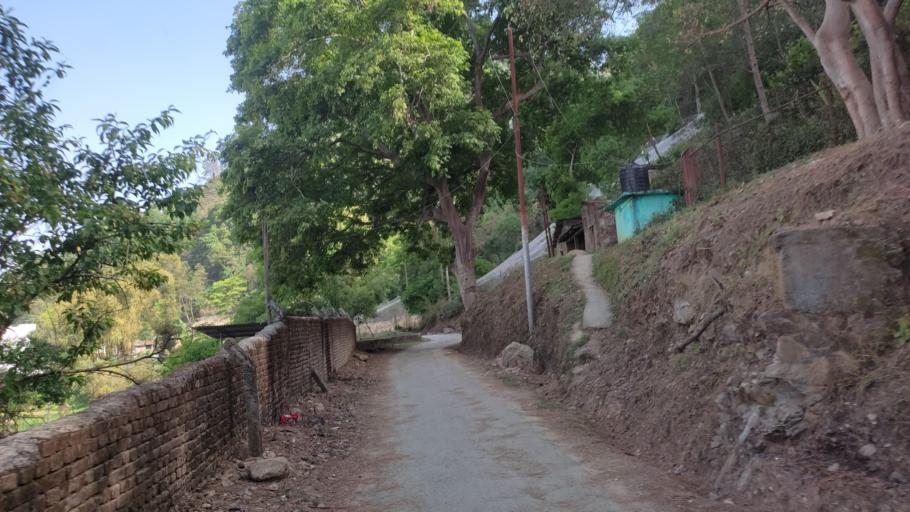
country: NP
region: Central Region
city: Kirtipur
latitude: 27.6578
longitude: 85.2646
